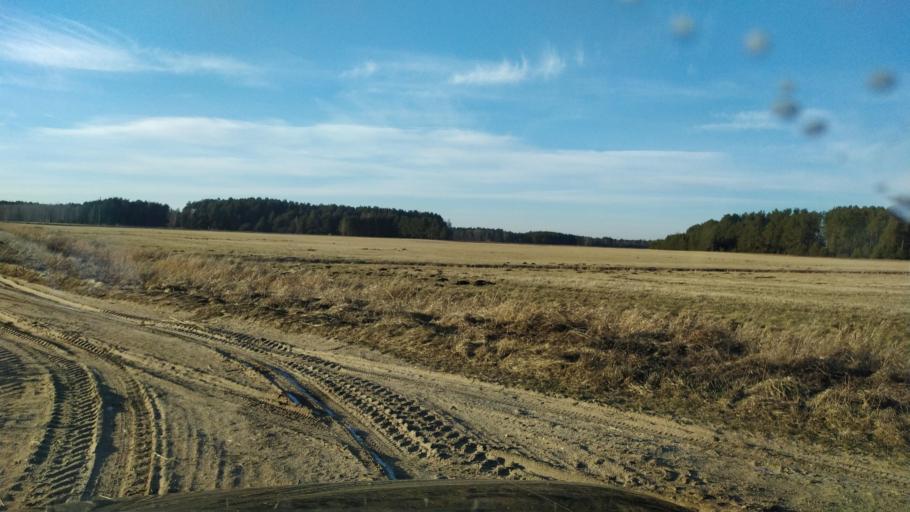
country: BY
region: Brest
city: Pruzhany
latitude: 52.5530
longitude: 24.3026
